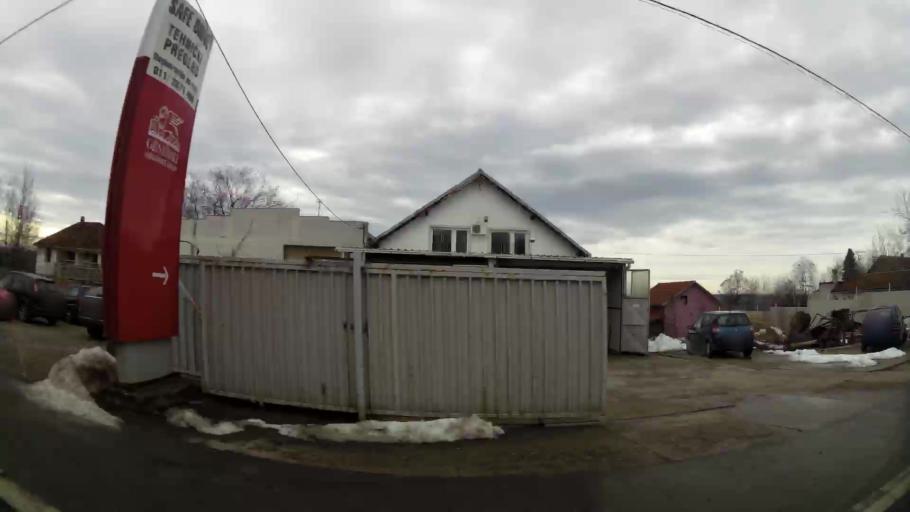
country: RS
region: Central Serbia
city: Sremcica
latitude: 44.7249
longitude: 20.3937
